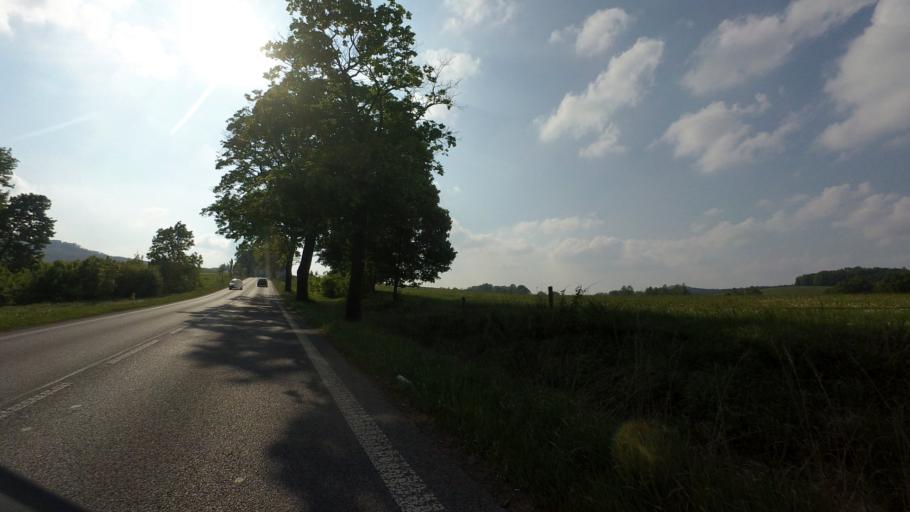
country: CZ
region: Ustecky
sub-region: Okres Decin
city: Sluknov
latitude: 51.0035
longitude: 14.4268
